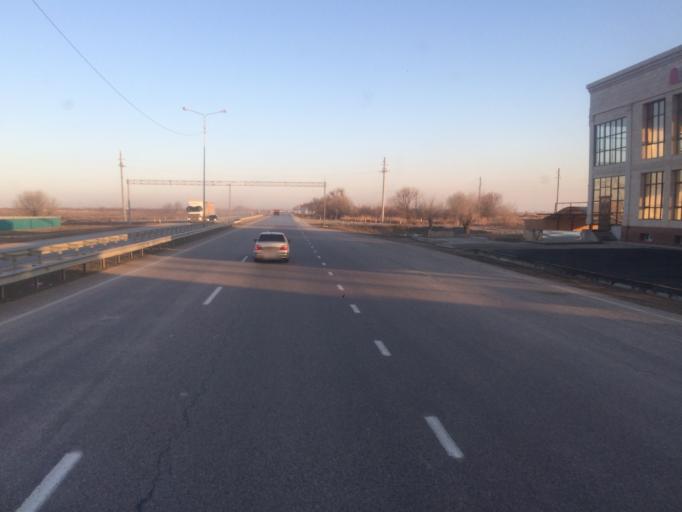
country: KZ
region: Ongtustik Qazaqstan
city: Turkestan
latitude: 43.2723
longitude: 68.3439
